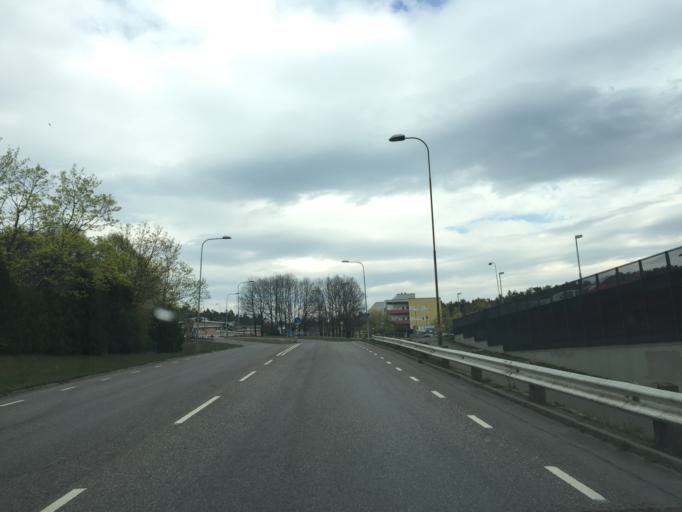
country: SE
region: Vaestra Goetaland
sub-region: Goteborg
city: Loevgaerdet
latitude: 57.8138
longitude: 12.0403
